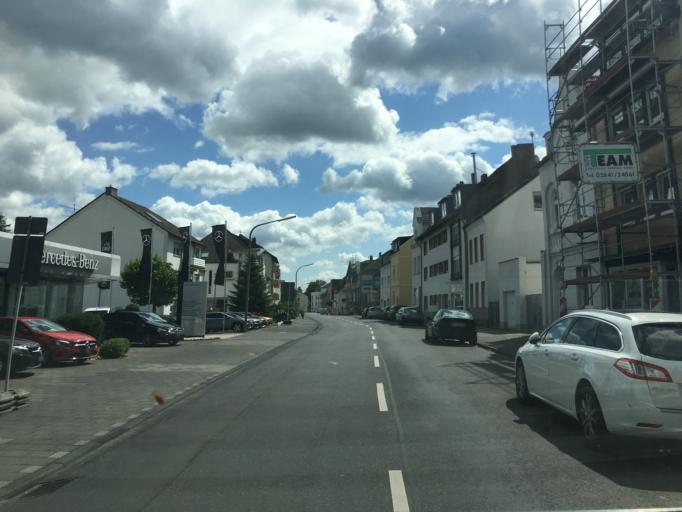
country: DE
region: Rheinland-Pfalz
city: Bad Neuenahr-Ahrweiler
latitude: 50.5449
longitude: 7.1262
